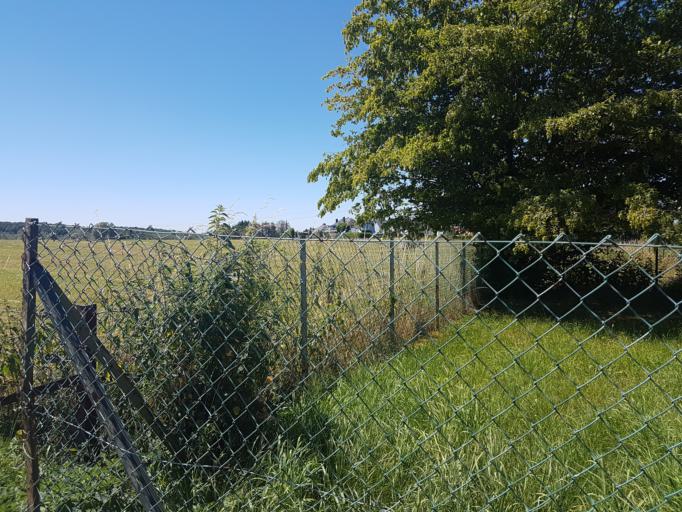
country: LU
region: Luxembourg
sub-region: Canton d'Esch-sur-Alzette
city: Leudelange
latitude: 49.5835
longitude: 6.1004
